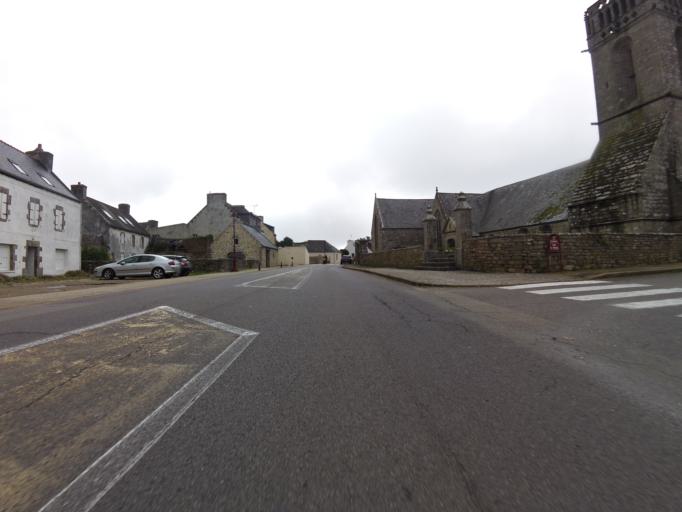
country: FR
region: Brittany
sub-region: Departement du Finistere
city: Plouhinec
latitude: 48.0143
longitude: -4.4862
